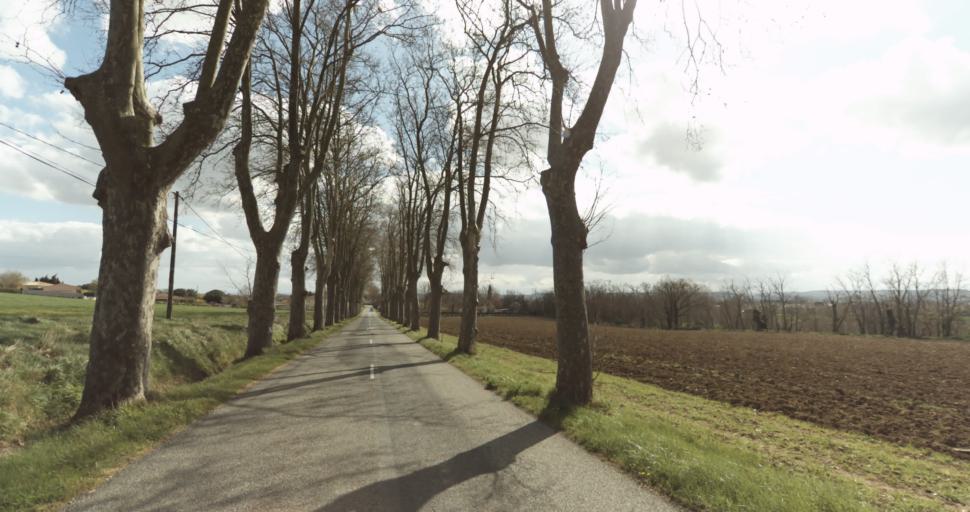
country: FR
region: Midi-Pyrenees
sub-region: Departement de la Haute-Garonne
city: Auterive
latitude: 43.3624
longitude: 1.4761
